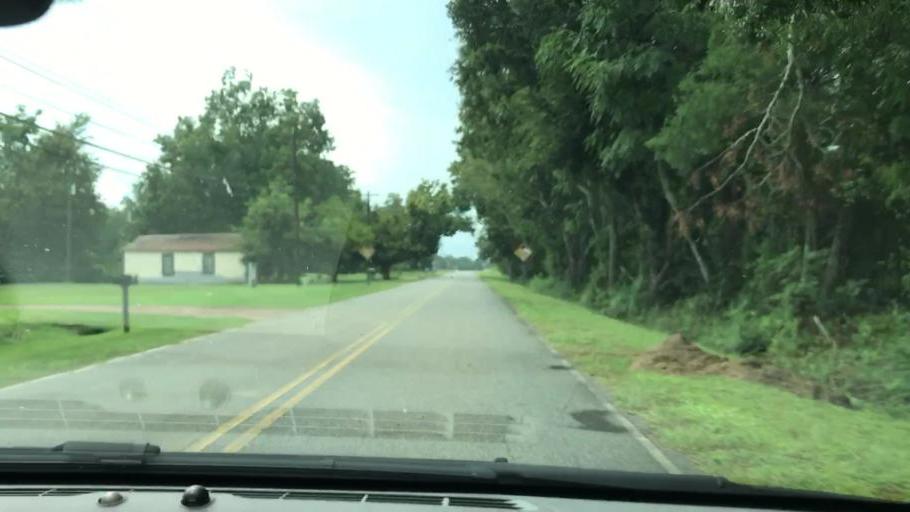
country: US
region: Georgia
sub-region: Early County
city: Blakely
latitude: 31.3749
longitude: -84.9542
